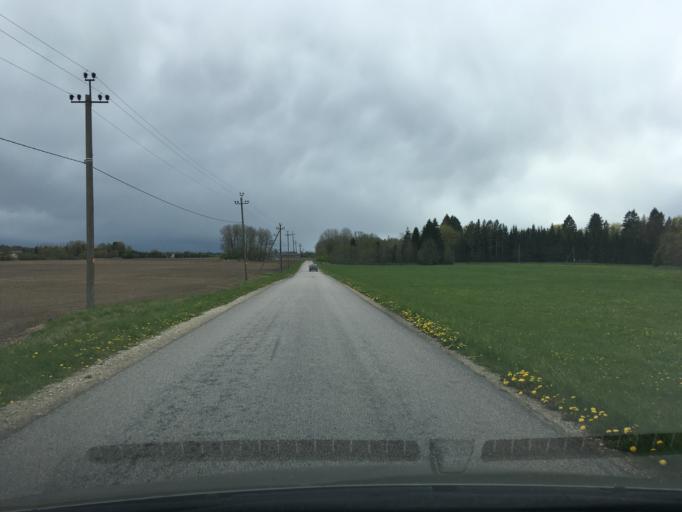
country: EE
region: Harju
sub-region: Joelaehtme vald
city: Loo
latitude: 59.3793
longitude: 24.9661
